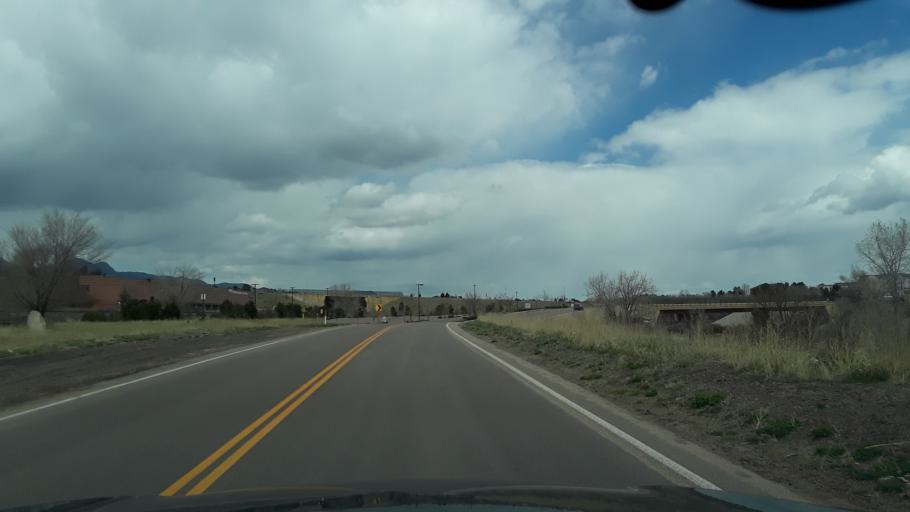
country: US
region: Colorado
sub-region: El Paso County
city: Air Force Academy
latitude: 38.9289
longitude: -104.8157
